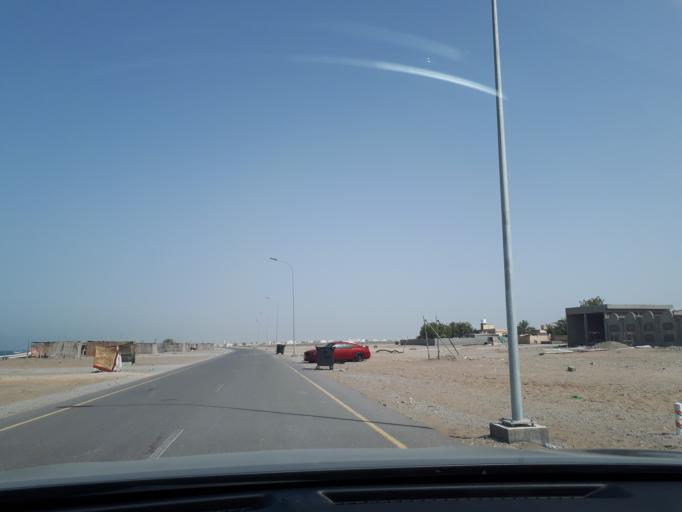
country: OM
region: Al Batinah
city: Barka'
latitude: 23.7291
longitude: 57.8391
